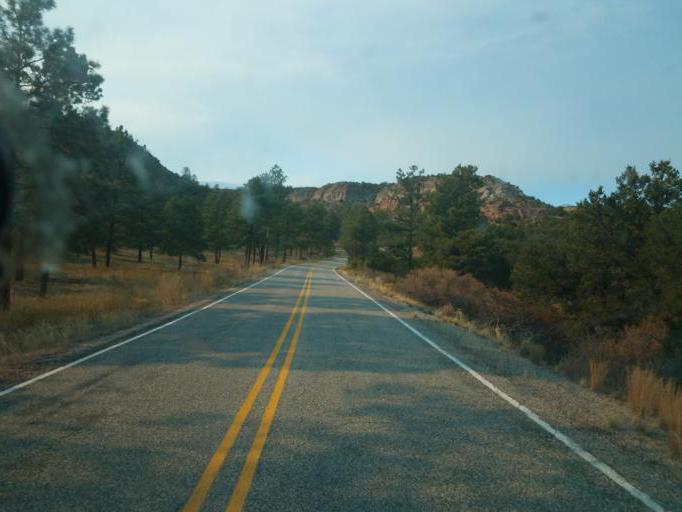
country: US
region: New Mexico
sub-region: Los Alamos County
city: White Rock
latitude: 35.8039
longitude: -106.2462
